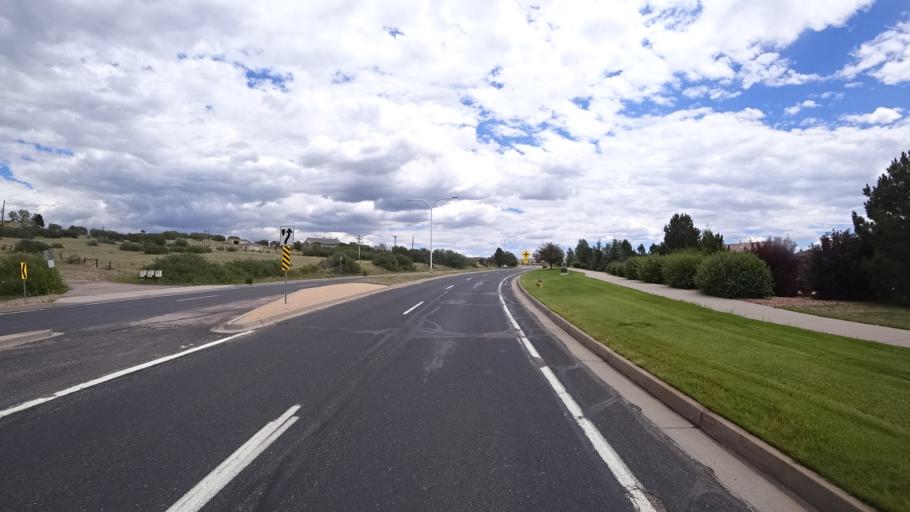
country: US
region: Colorado
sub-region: El Paso County
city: Gleneagle
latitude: 39.0279
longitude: -104.8026
